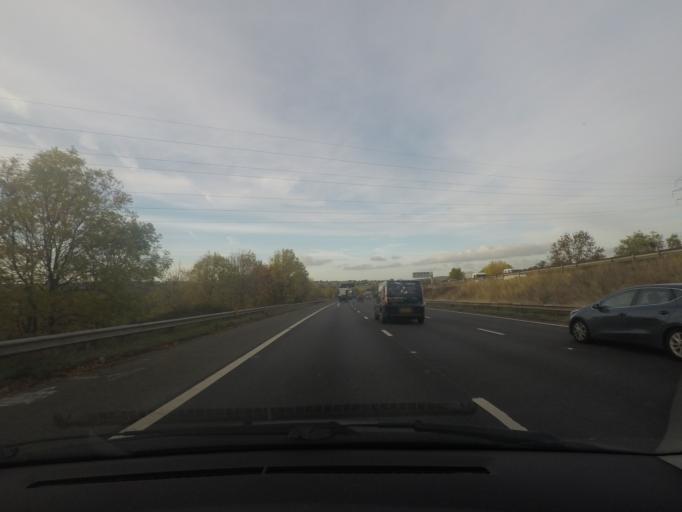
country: GB
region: England
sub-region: Barnsley
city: Darton
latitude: 53.5670
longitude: -1.5405
